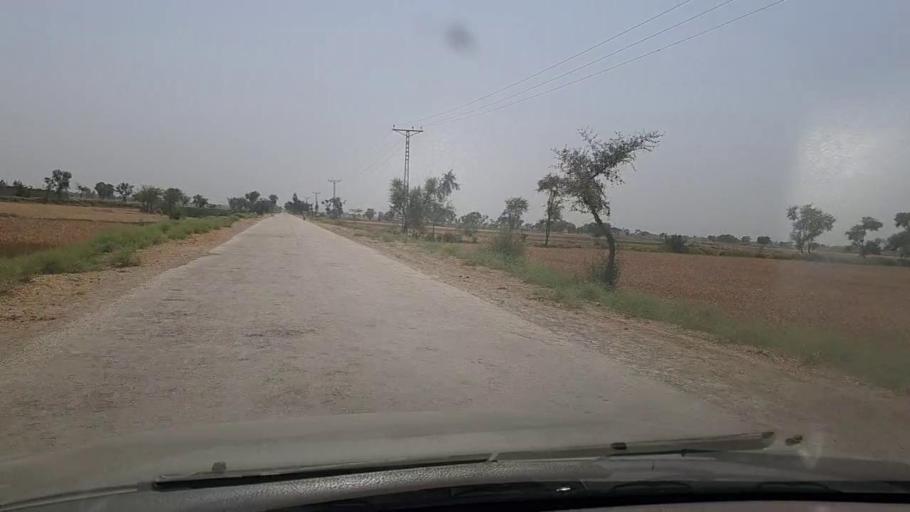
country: PK
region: Sindh
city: Miro Khan
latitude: 27.7126
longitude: 68.0656
